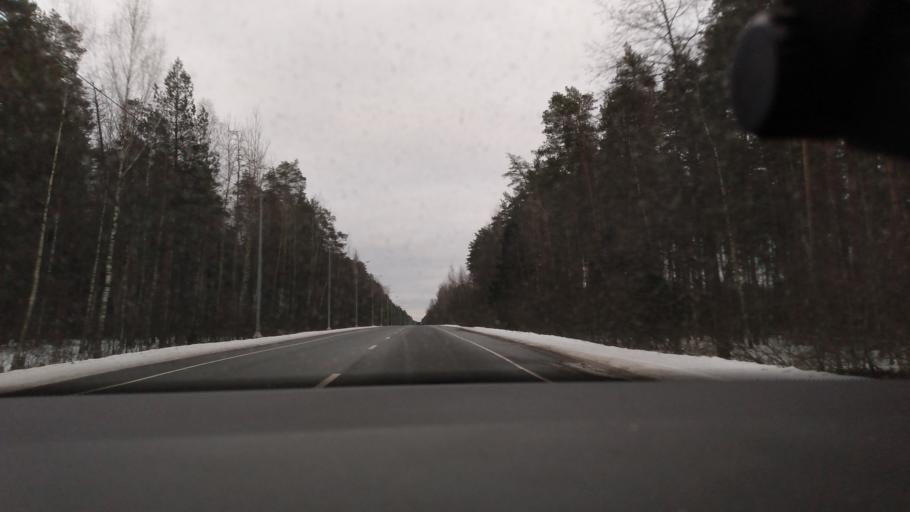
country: RU
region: Moskovskaya
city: Il'inskiy Pogost
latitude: 55.4660
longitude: 38.9717
